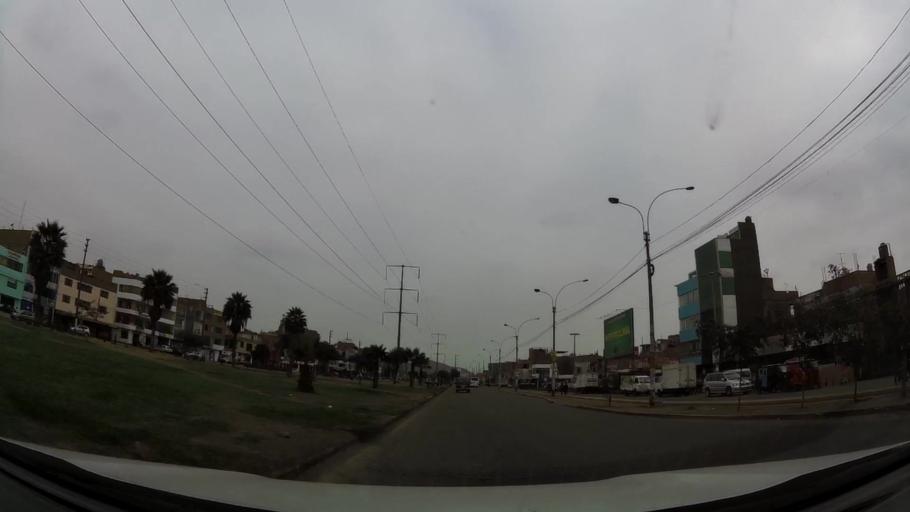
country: PE
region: Lima
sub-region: Lima
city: Independencia
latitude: -11.9805
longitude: -77.0780
